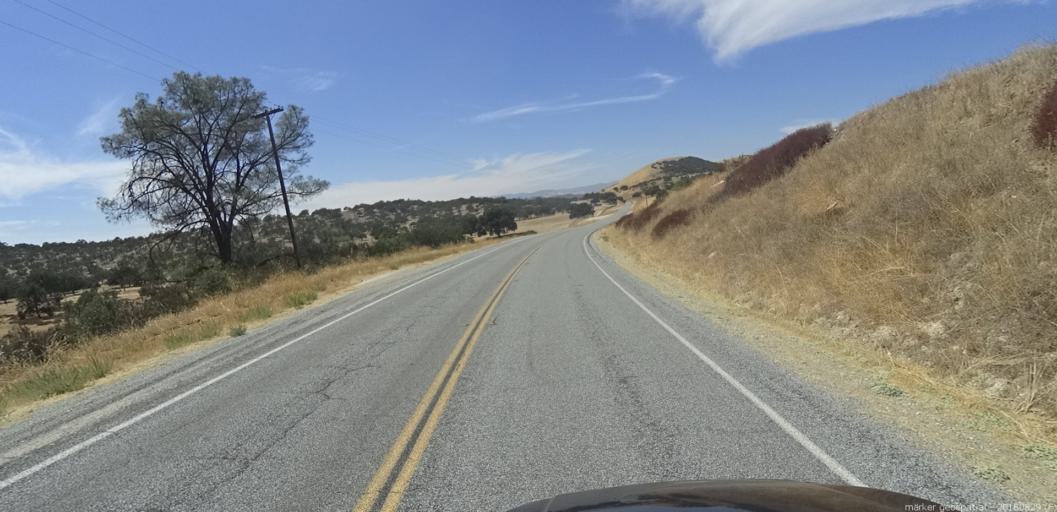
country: US
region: California
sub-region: San Luis Obispo County
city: Lake Nacimiento
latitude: 35.9063
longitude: -120.9953
